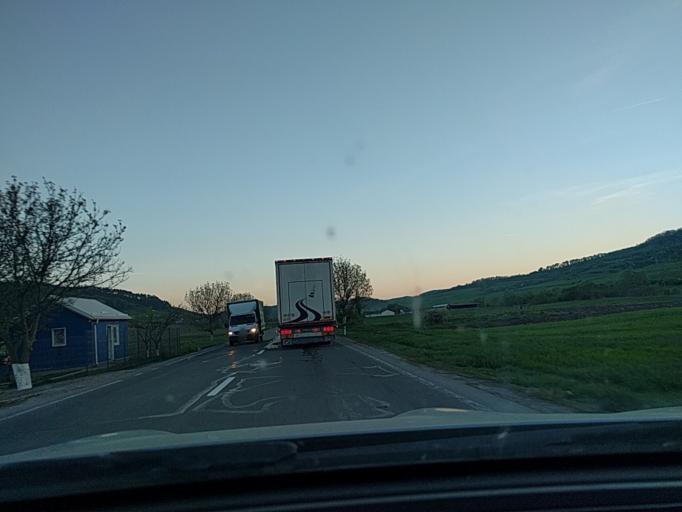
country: RO
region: Mures
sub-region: Comuna Balauseri
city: Chendu
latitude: 46.3649
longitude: 24.7220
